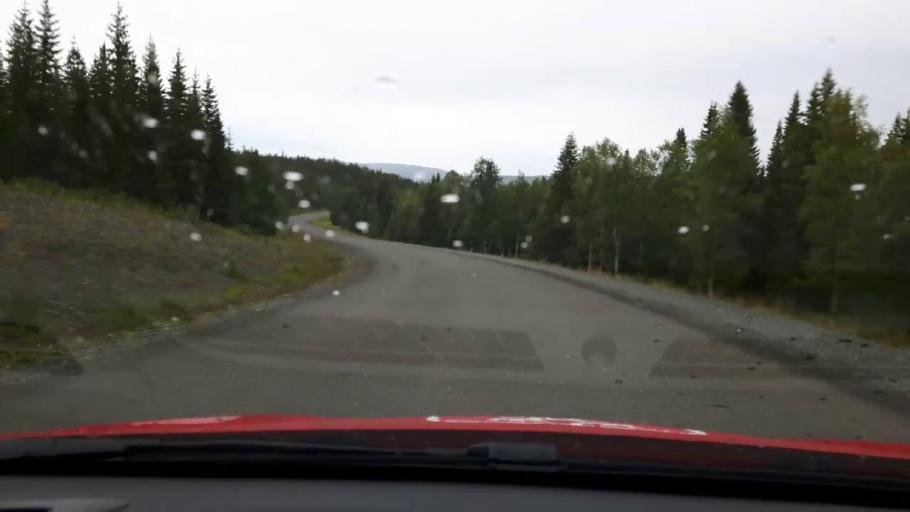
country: SE
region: Jaemtland
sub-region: Are Kommun
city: Are
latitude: 63.4158
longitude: 12.7591
